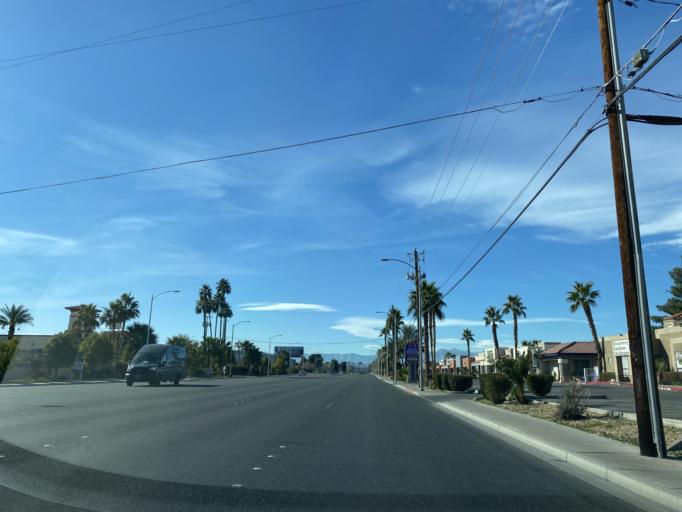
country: US
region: Nevada
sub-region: Clark County
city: Sunrise Manor
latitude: 36.1741
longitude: -115.0648
